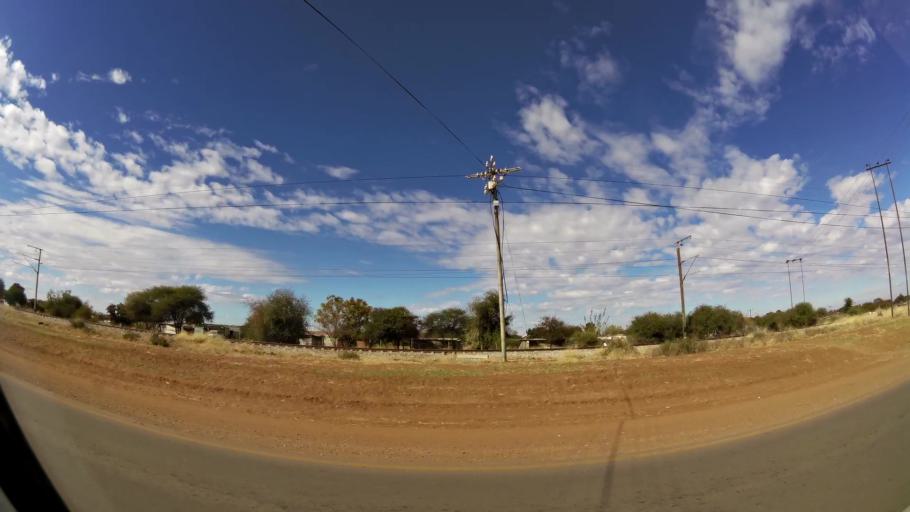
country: ZA
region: Limpopo
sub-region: Waterberg District Municipality
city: Bela-Bela
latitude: -24.8796
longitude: 28.3099
